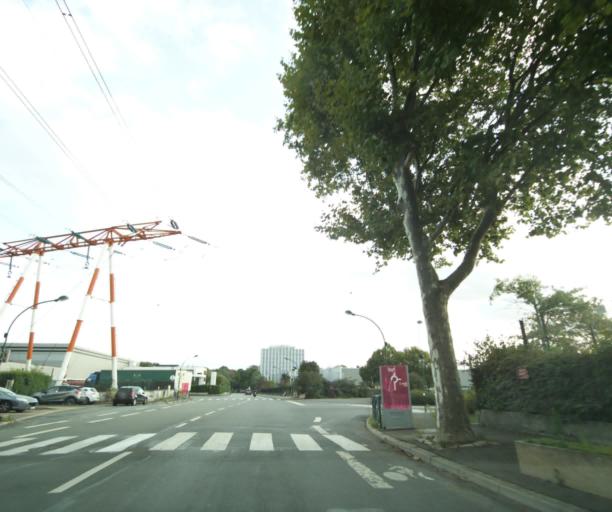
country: FR
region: Ile-de-France
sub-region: Departement des Hauts-de-Seine
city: Chatenay-Malabry
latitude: 48.7758
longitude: 2.2454
